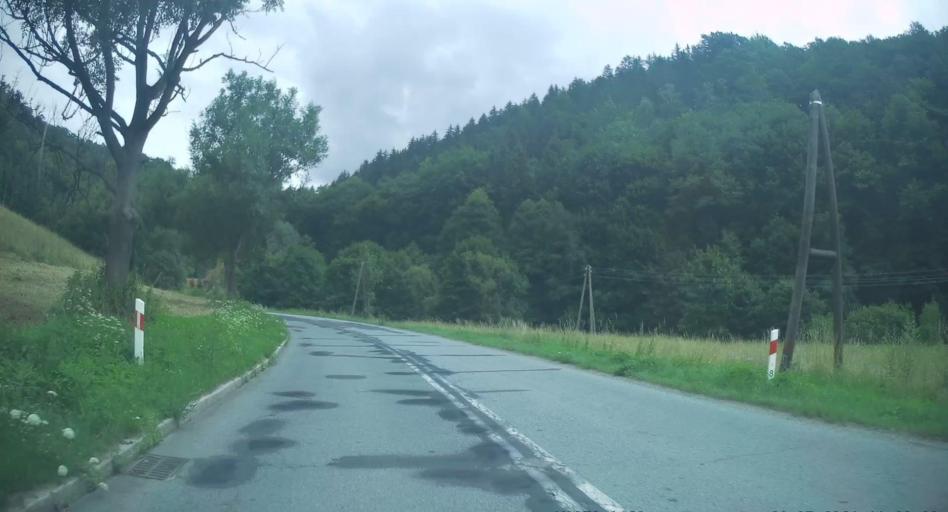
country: PL
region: Lower Silesian Voivodeship
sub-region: Powiat walbrzyski
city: Jedlina-Zdroj
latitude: 50.7280
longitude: 16.3876
